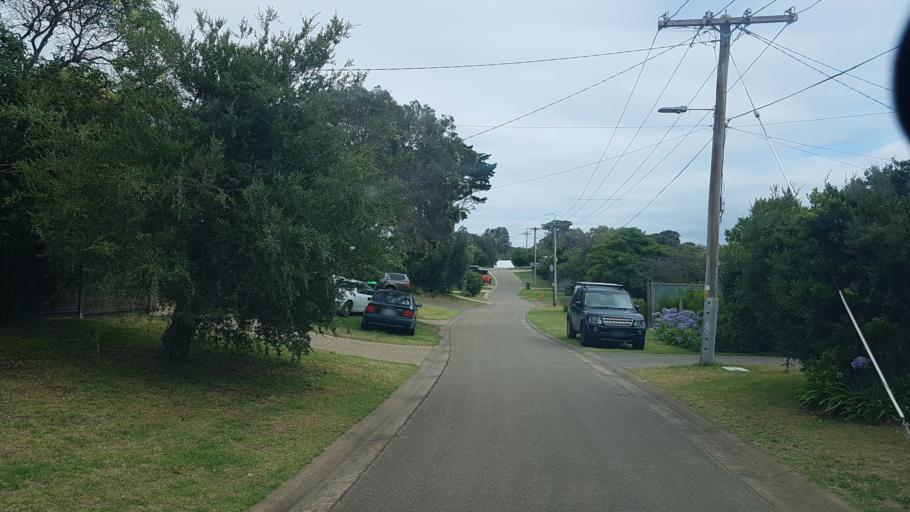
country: AU
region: Victoria
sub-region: Mornington Peninsula
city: Blairgowrie
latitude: -38.3599
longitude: 144.7608
